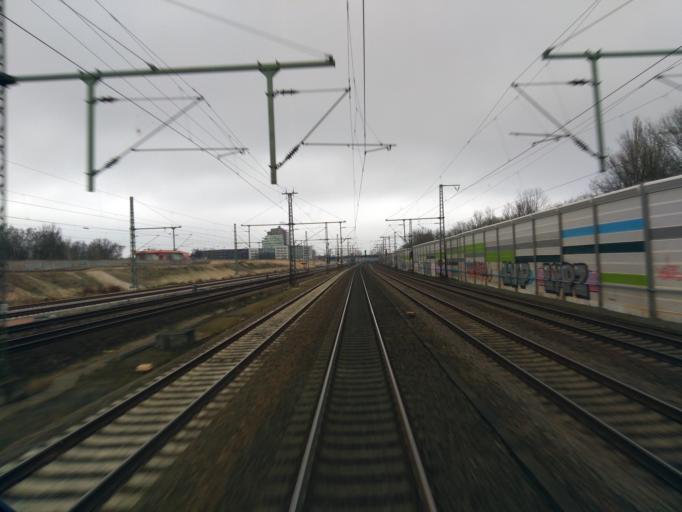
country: DE
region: Hamburg
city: Harburg
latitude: 53.4906
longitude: 10.0047
